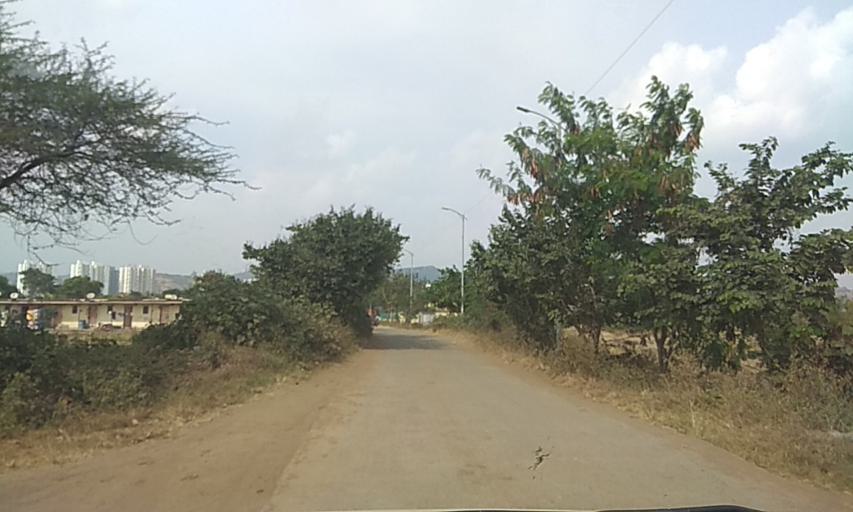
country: IN
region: Maharashtra
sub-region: Pune Division
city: Pimpri
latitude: 18.5806
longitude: 73.7075
